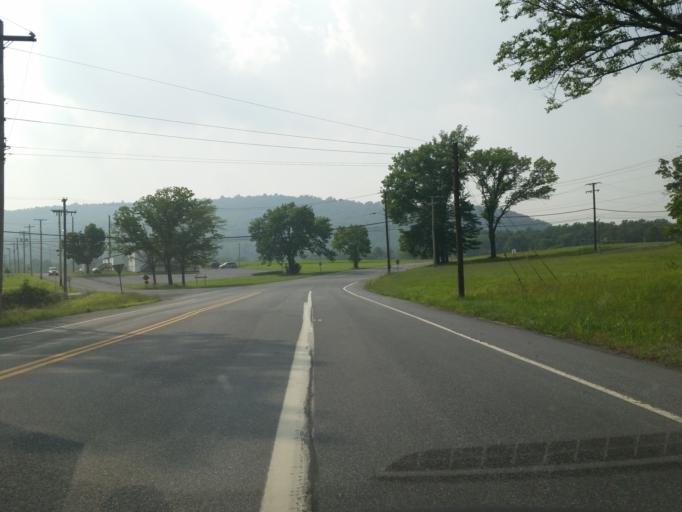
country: US
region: Pennsylvania
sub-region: Lebanon County
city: Jonestown
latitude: 40.4283
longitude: -76.5896
